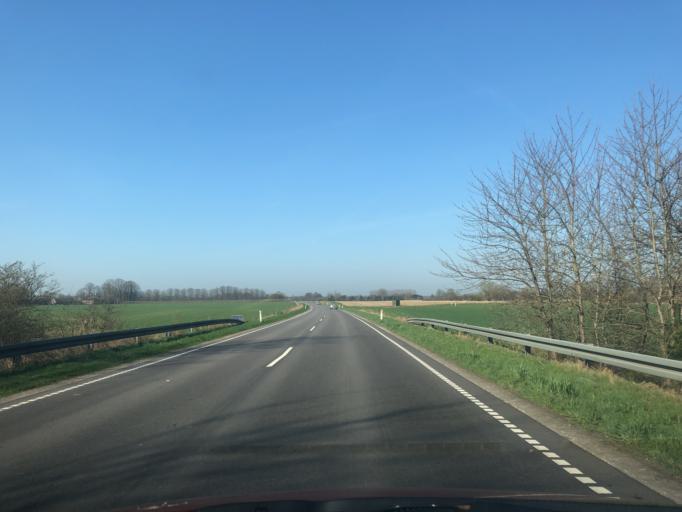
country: DK
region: Zealand
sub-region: Faxe Kommune
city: Fakse
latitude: 55.2781
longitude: 12.1631
